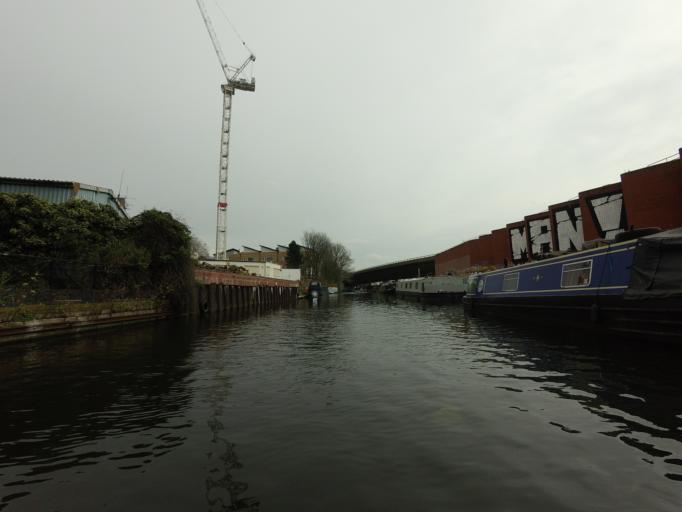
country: GB
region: England
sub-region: Greater London
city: Bayswater
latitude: 51.5223
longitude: -0.2003
